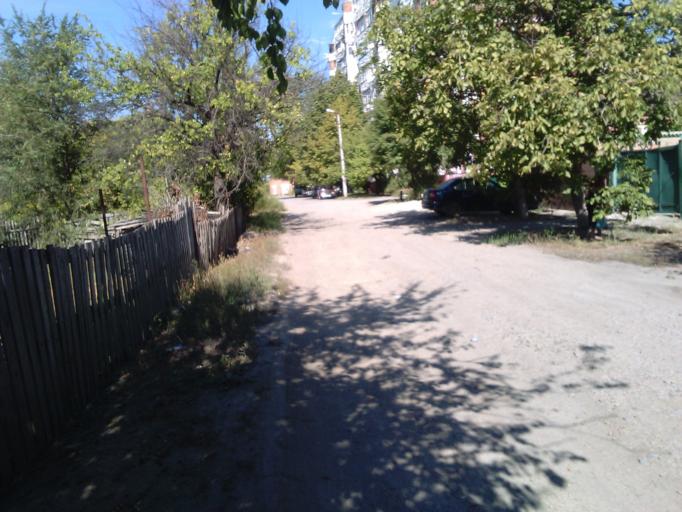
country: RU
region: Rostov
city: Bataysk
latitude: 47.1194
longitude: 39.7328
